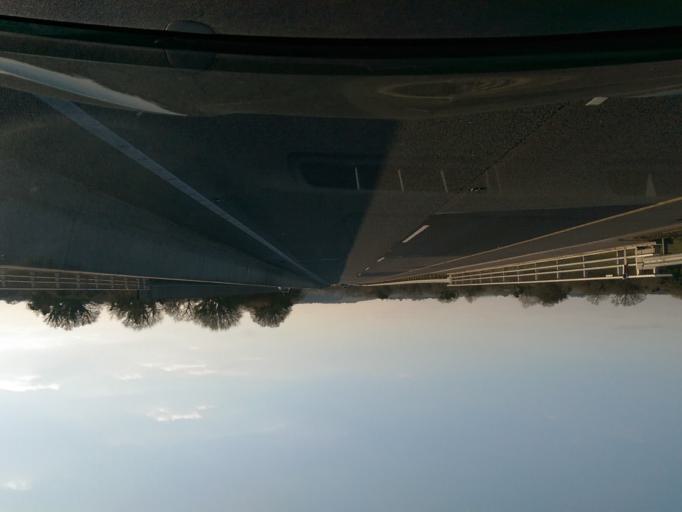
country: IE
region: Leinster
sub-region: Laois
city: Mountrath
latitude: 52.9538
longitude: -7.4430
